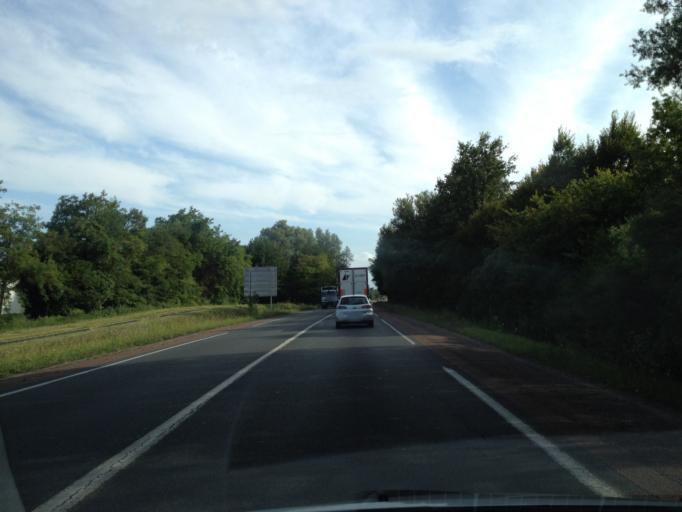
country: FR
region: Poitou-Charentes
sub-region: Departement de la Charente-Maritime
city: Rochefort
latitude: 45.9487
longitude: -0.9874
